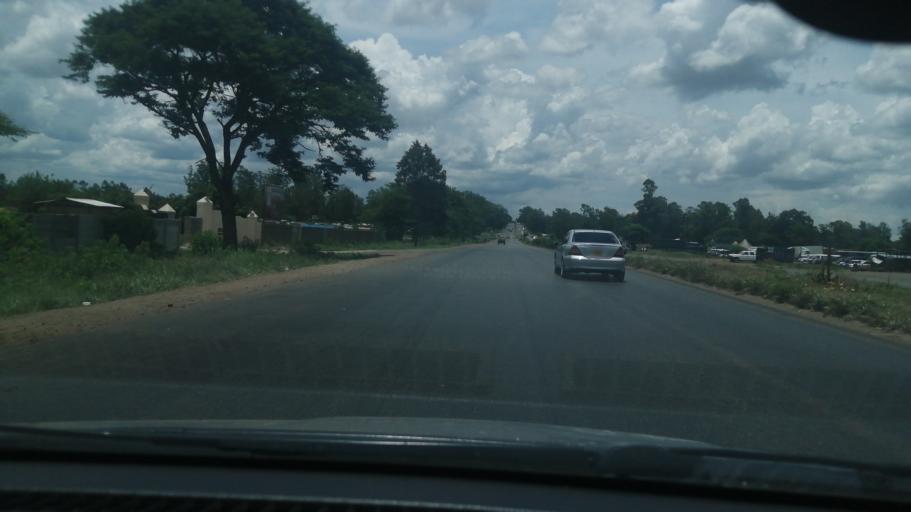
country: ZW
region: Harare
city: Harare
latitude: -17.8219
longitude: 30.9599
